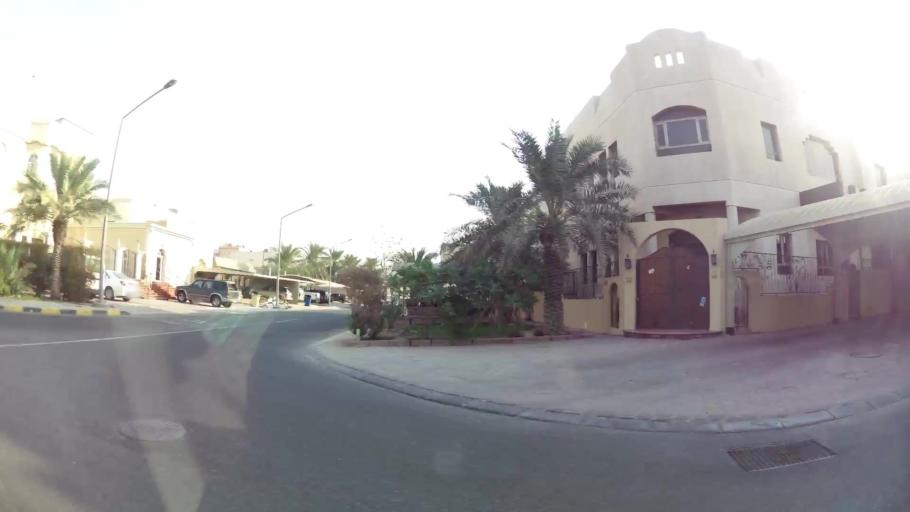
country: KW
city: Bayan
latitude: 29.3021
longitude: 48.0477
